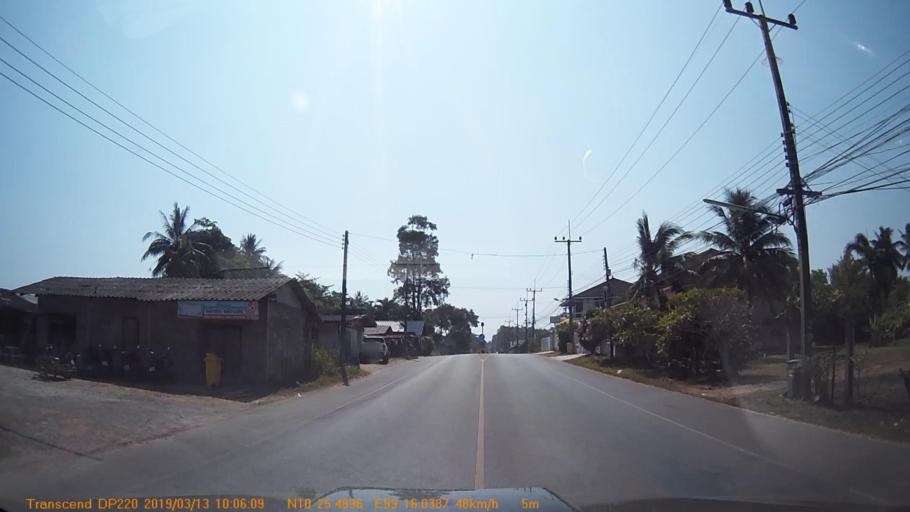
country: TH
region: Chumphon
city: Chumphon
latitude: 10.4247
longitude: 99.2675
